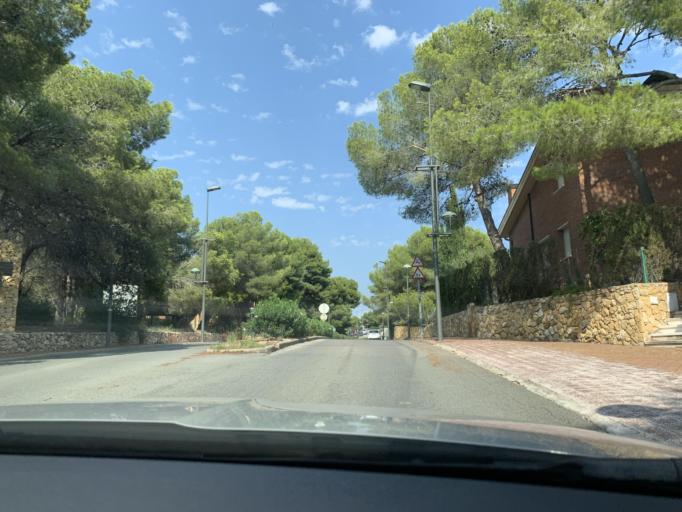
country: ES
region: Catalonia
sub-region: Provincia de Tarragona
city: Altafulla
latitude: 41.1313
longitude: 1.3542
